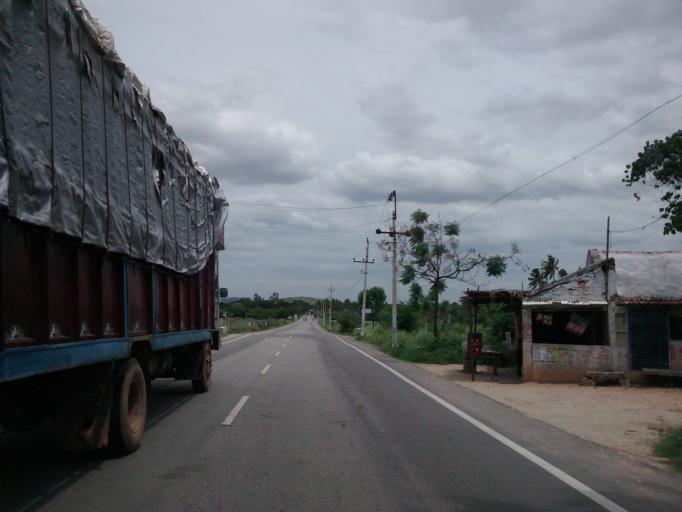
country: IN
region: Andhra Pradesh
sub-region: Chittoor
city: Chittoor
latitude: 13.2838
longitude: 79.0404
